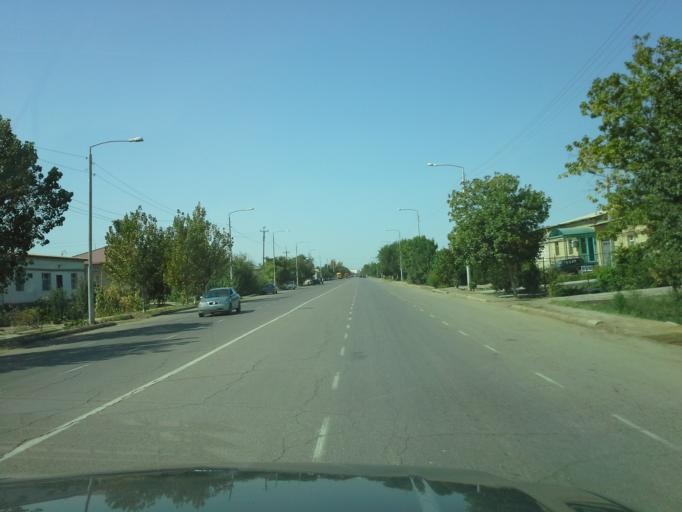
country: TM
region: Dasoguz
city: Dasoguz
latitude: 41.8129
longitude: 59.9901
